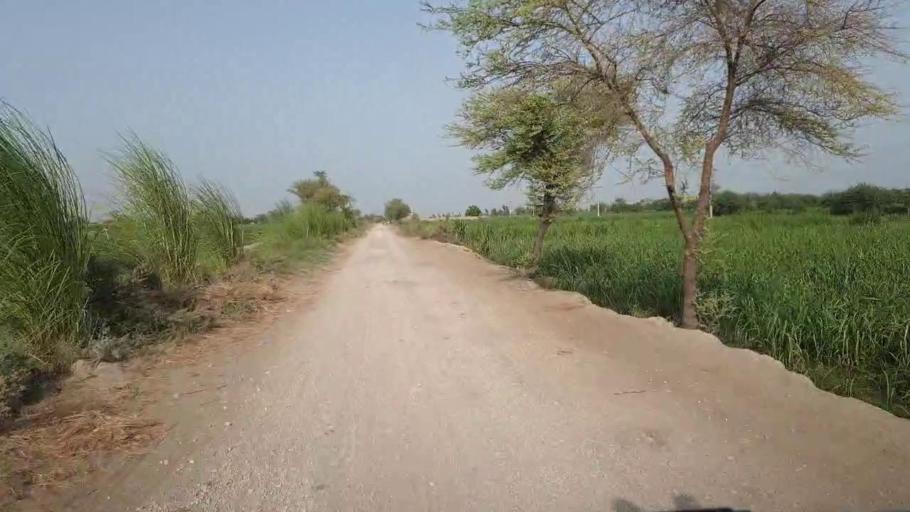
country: PK
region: Sindh
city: Daur
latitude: 26.3408
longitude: 68.1931
